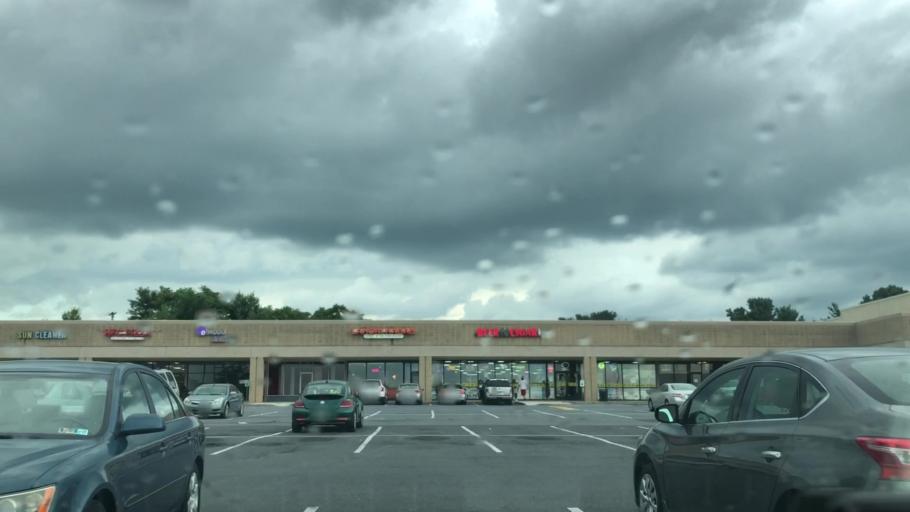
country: US
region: Pennsylvania
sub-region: Dauphin County
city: Progress
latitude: 40.2790
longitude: -76.8270
